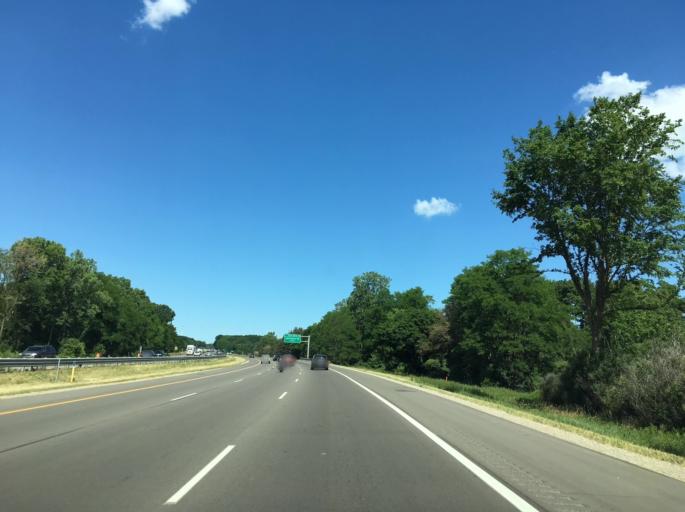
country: US
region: Michigan
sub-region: Oakland County
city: Clarkston
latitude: 42.7257
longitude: -83.3557
